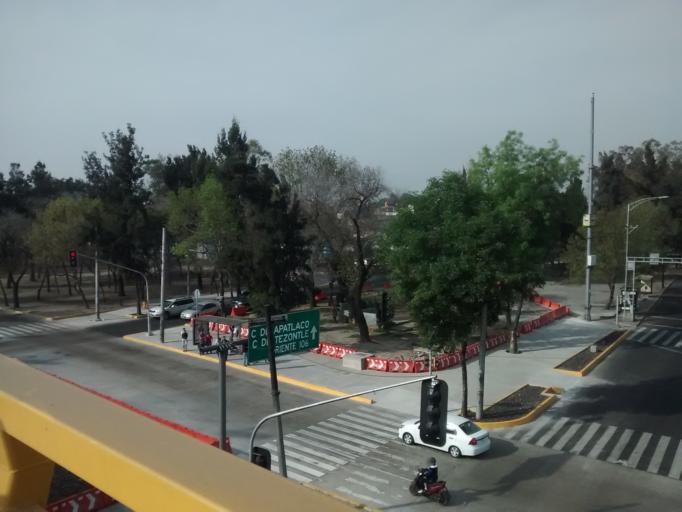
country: MX
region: Mexico City
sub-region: Iztacalco
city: Iztacalco
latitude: 19.3968
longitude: -99.0990
